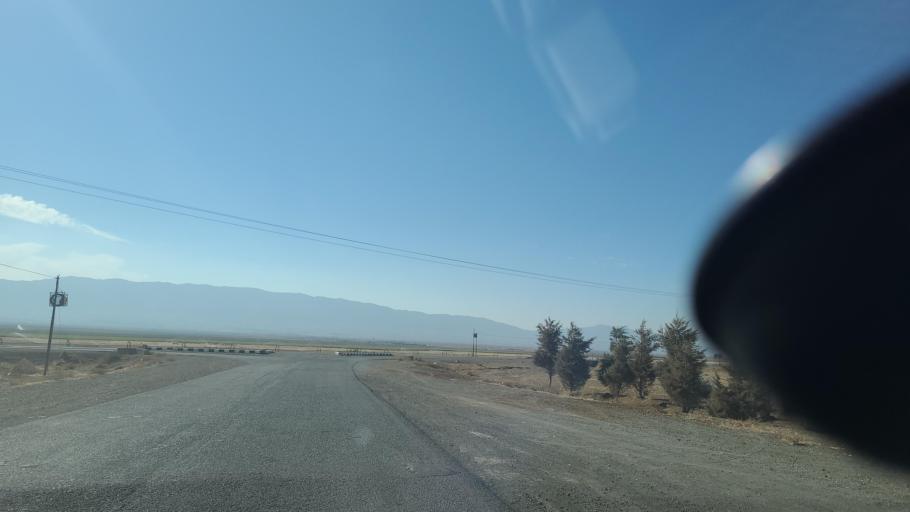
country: IR
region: Razavi Khorasan
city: Dowlatabad
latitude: 35.6009
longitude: 59.4605
